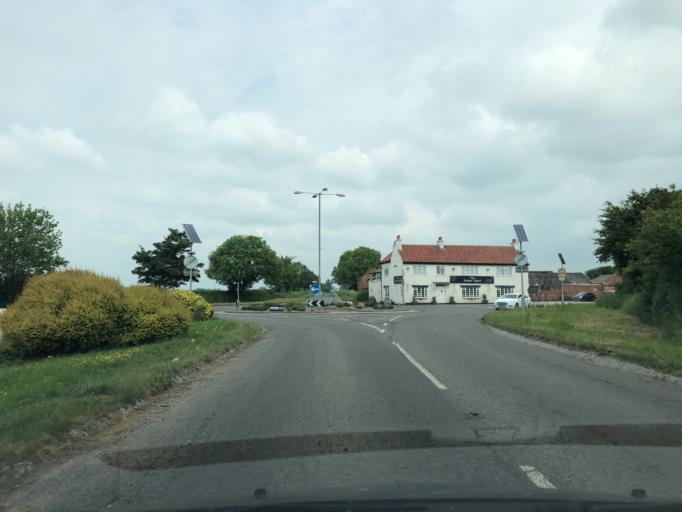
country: GB
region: England
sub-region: North Yorkshire
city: Thirsk
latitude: 54.2211
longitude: -1.4146
